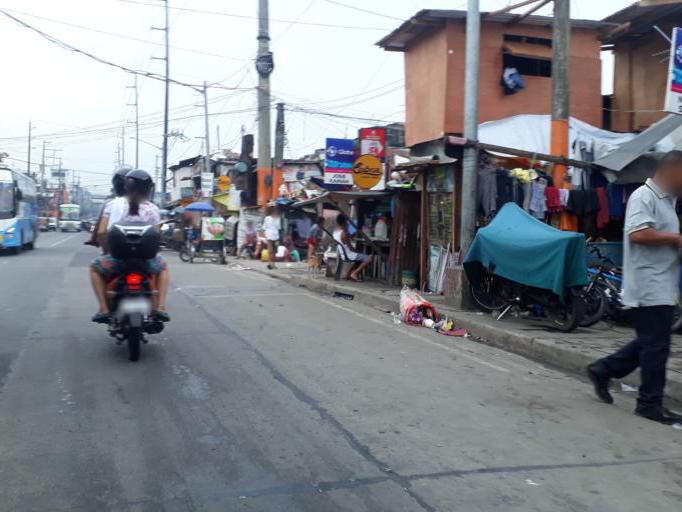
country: PH
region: Metro Manila
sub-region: Caloocan City
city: Niugan
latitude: 14.6586
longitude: 120.9670
